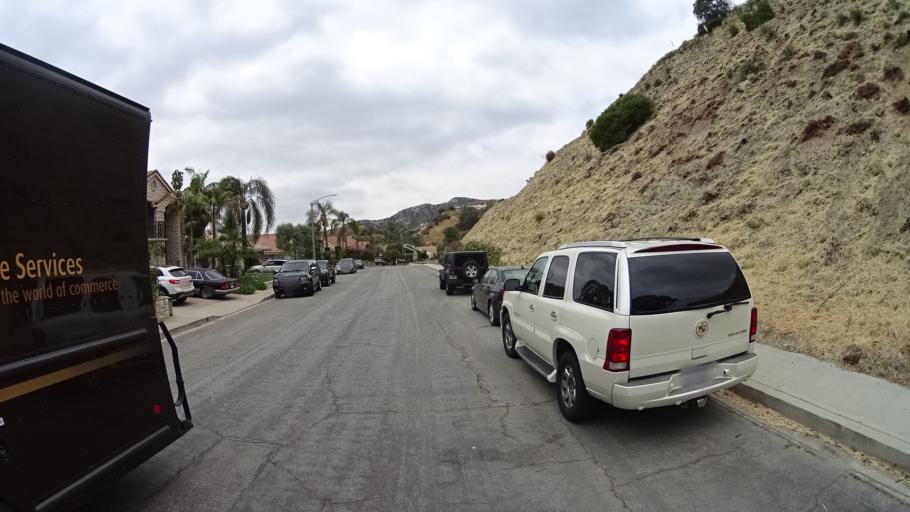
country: US
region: California
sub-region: Los Angeles County
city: Burbank
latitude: 34.2108
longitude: -118.3253
